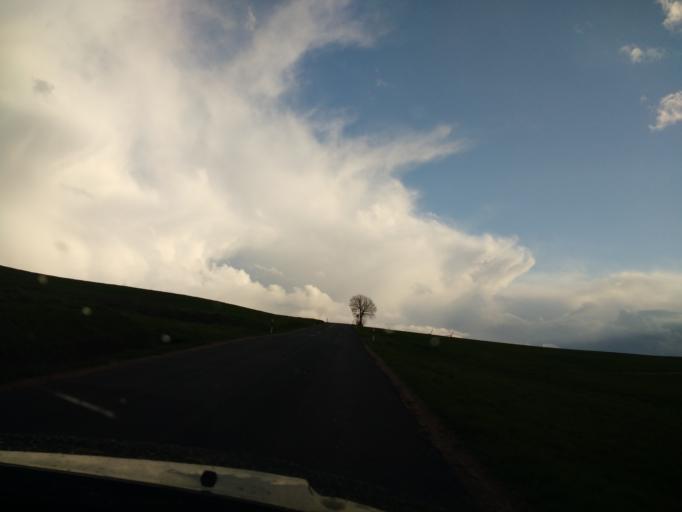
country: DE
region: Rheinland-Pfalz
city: Basberg
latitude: 50.2822
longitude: 6.6115
